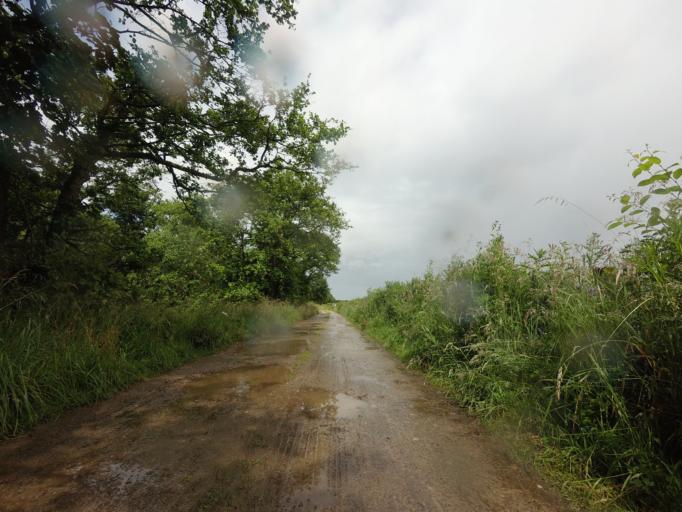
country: GB
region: Scotland
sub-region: Moray
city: Fochabers
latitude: 57.6635
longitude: -3.0907
